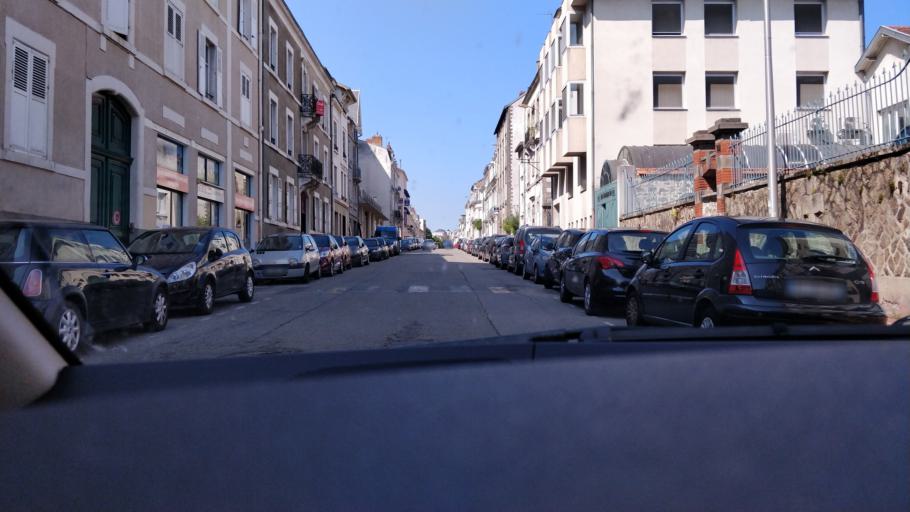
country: FR
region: Limousin
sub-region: Departement de la Haute-Vienne
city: Limoges
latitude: 45.8362
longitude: 1.2625
